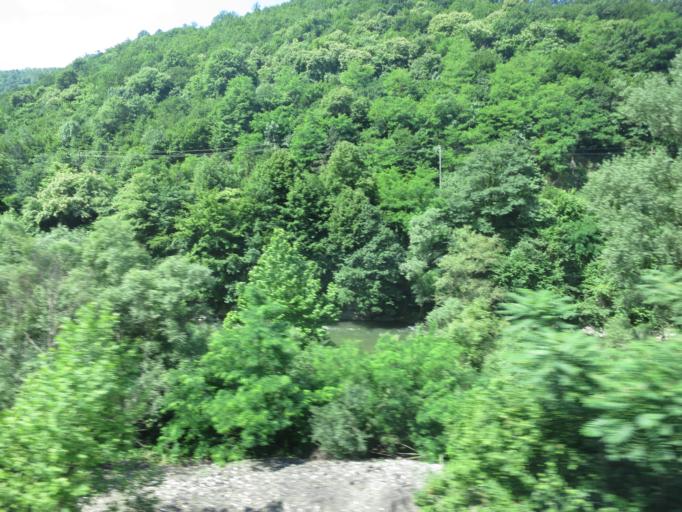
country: GE
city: Shorapani
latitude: 42.0896
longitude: 43.1414
